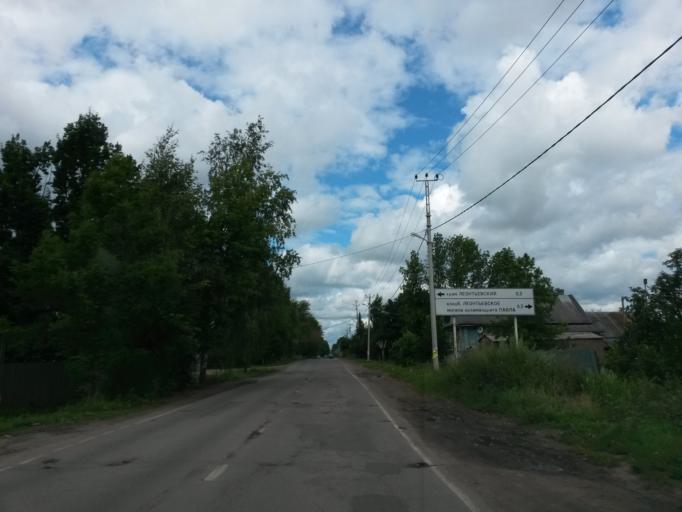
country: RU
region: Jaroslavl
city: Tutayev
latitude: 57.8788
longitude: 39.5589
